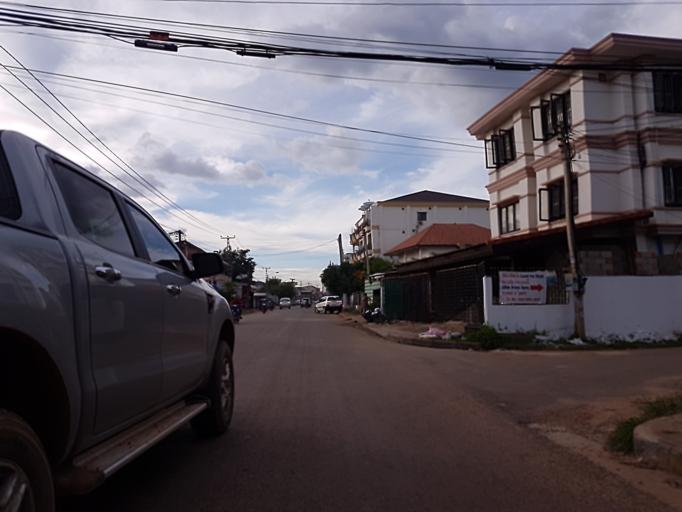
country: LA
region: Vientiane
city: Vientiane
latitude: 17.9790
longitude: 102.5874
